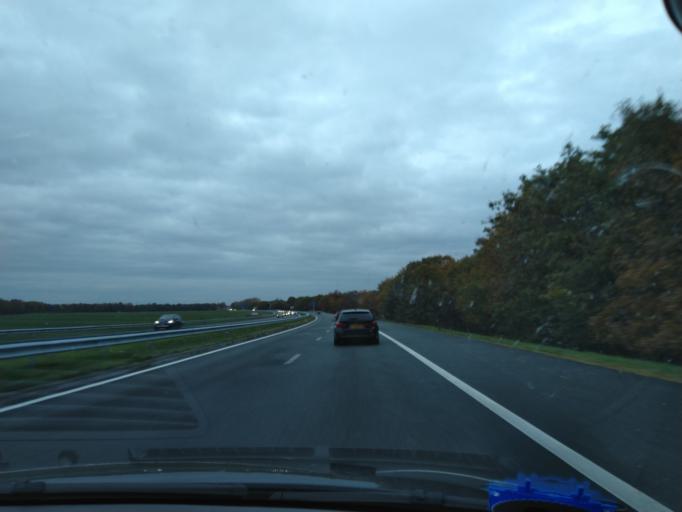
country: NL
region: Drenthe
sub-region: Gemeente Tynaarlo
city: Tynaarlo
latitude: 53.0641
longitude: 6.6031
